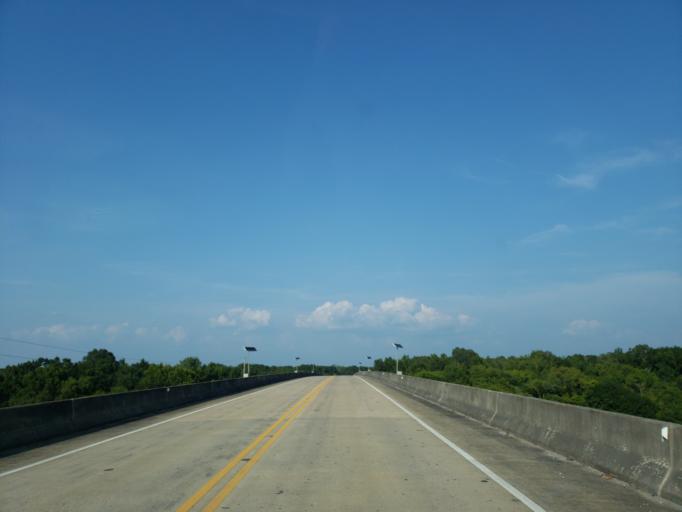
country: US
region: Alabama
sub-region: Sumter County
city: Livingston
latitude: 32.6941
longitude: -88.1152
